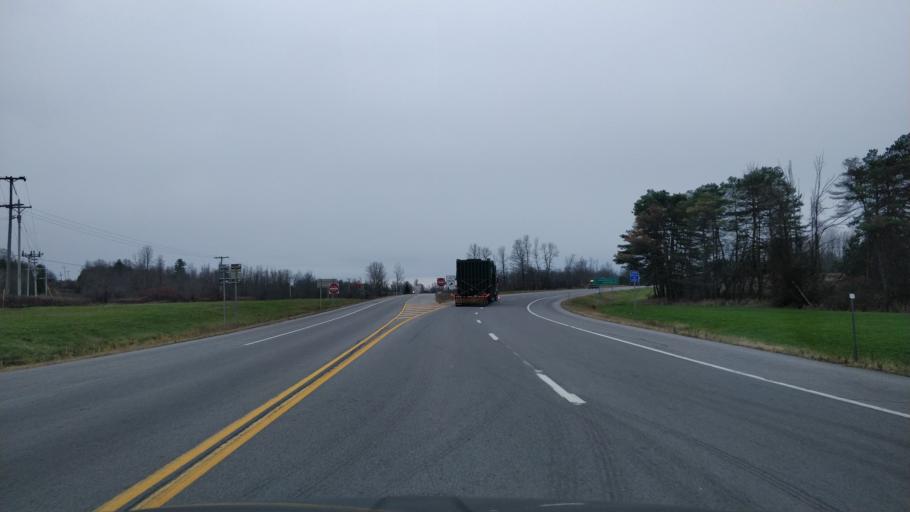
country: CA
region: Ontario
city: Brockville
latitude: 44.5786
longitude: -75.6411
